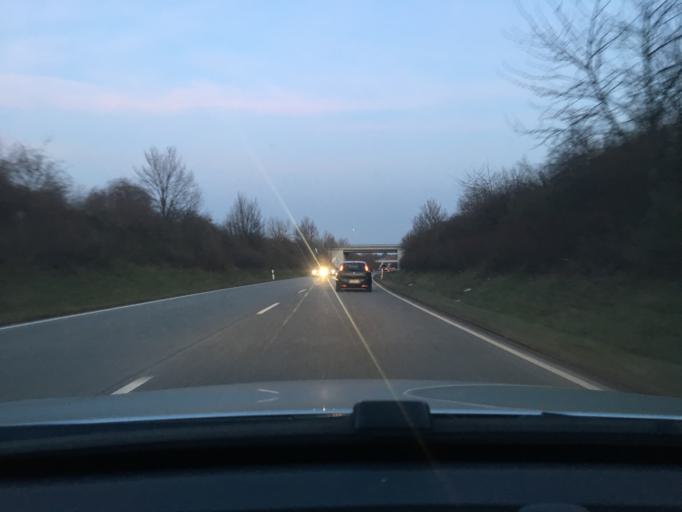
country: DE
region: Rheinland-Pfalz
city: Neustadt
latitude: 49.3613
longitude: 8.1606
